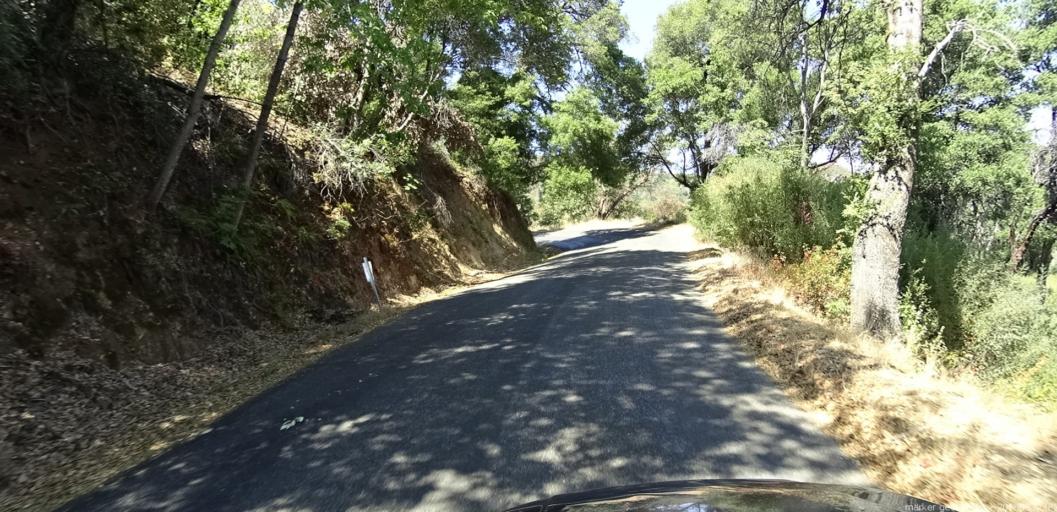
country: US
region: California
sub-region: Monterey County
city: Greenfield
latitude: 36.0116
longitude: -121.4448
